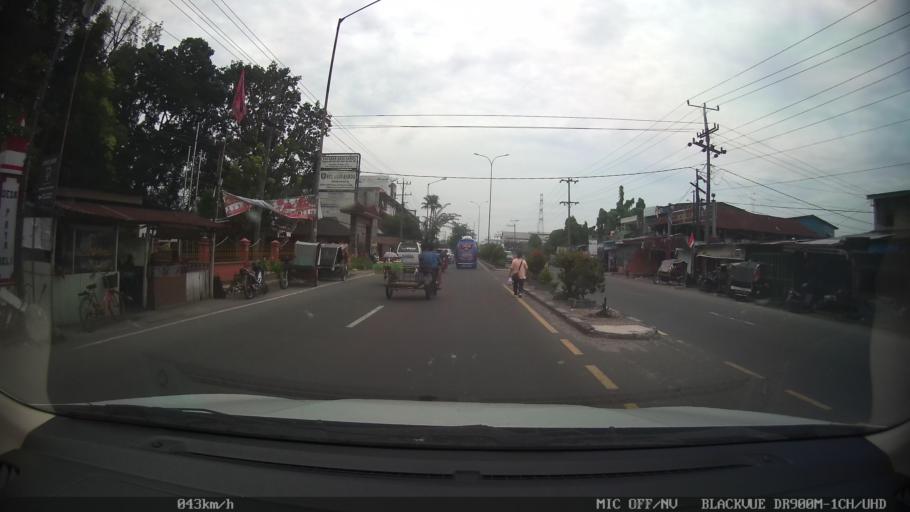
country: ID
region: North Sumatra
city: Sunggal
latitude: 3.5990
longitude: 98.5908
